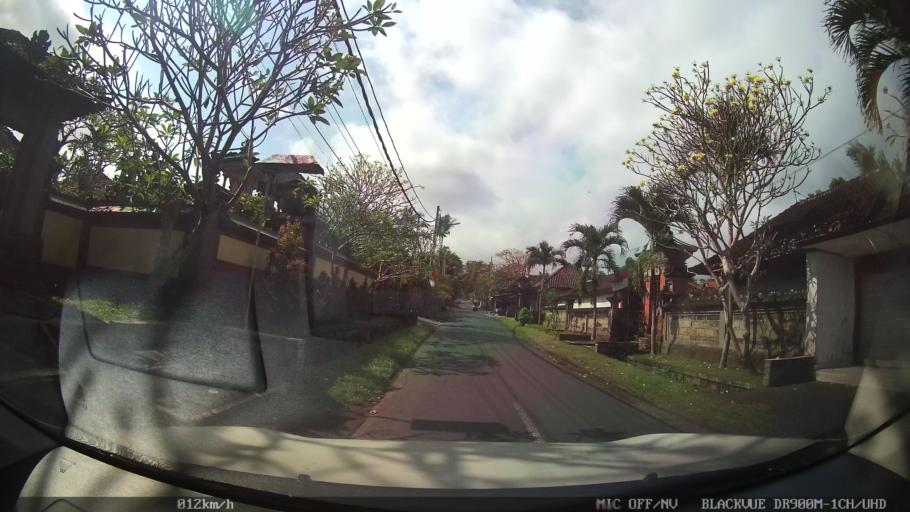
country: ID
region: Bali
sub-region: Kabupaten Gianyar
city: Ubud
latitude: -8.5125
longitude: 115.2909
